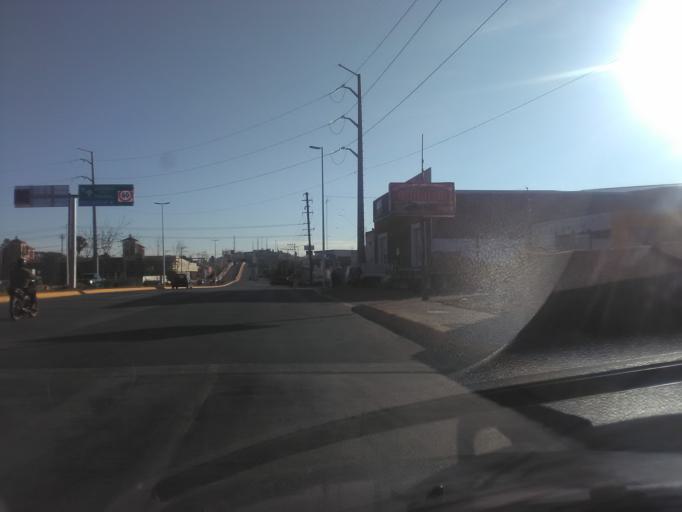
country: MX
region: Durango
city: Victoria de Durango
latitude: 24.0053
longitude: -104.6959
